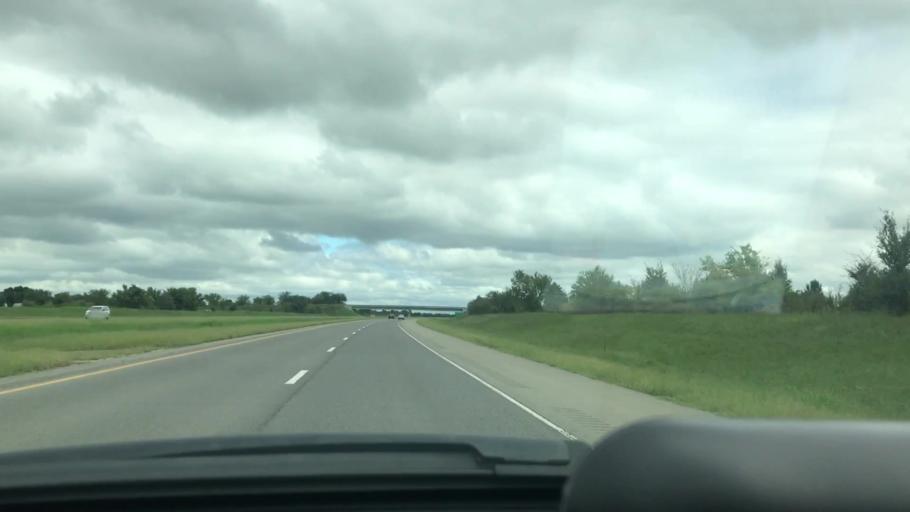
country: US
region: Oklahoma
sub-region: McIntosh County
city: Checotah
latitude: 35.5906
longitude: -95.4875
